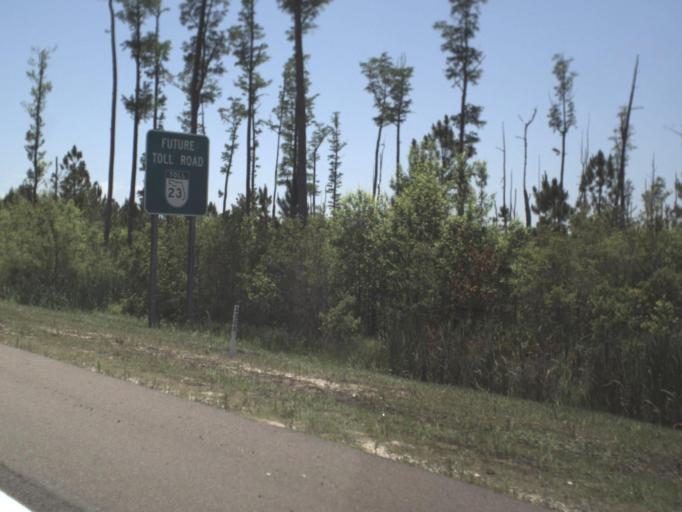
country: US
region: Florida
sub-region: Duval County
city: Baldwin
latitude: 30.2731
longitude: -81.8748
